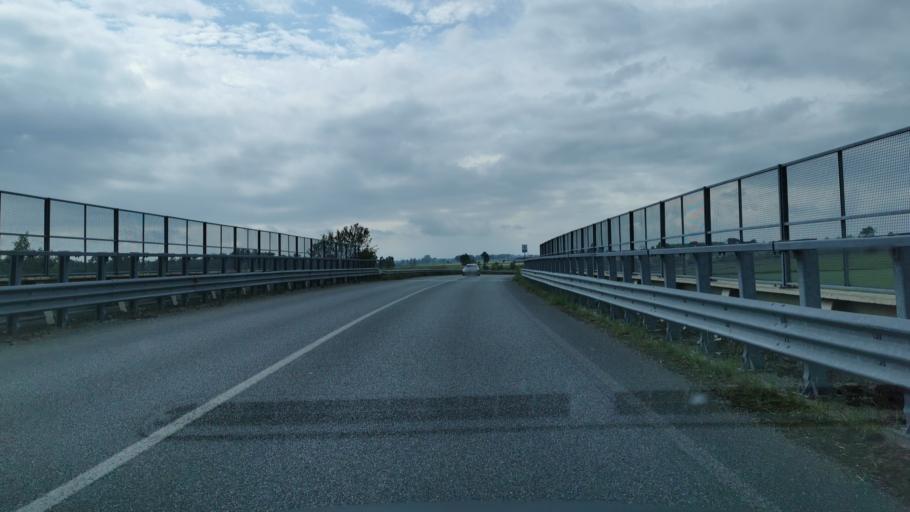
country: IT
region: Piedmont
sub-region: Provincia di Cuneo
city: Racconigi
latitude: 44.7951
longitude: 7.6997
